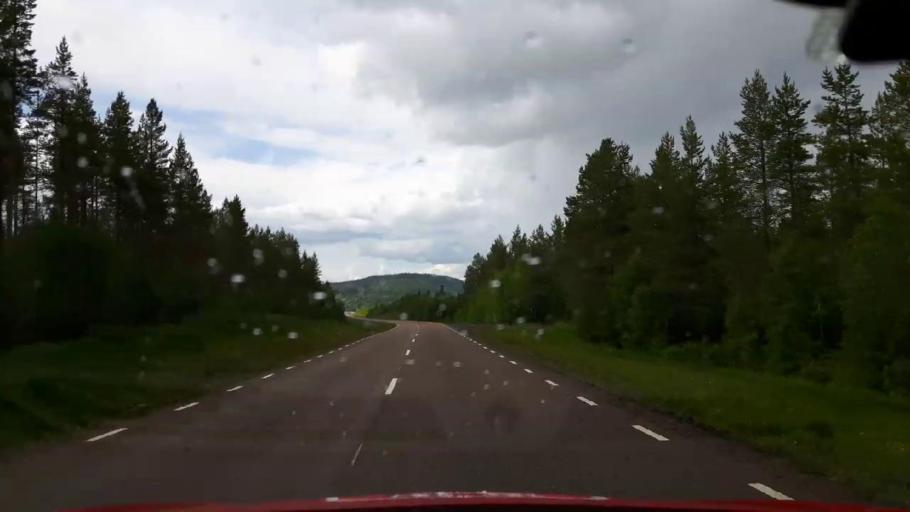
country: SE
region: Jaemtland
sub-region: Krokoms Kommun
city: Valla
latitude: 63.8942
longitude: 14.2602
